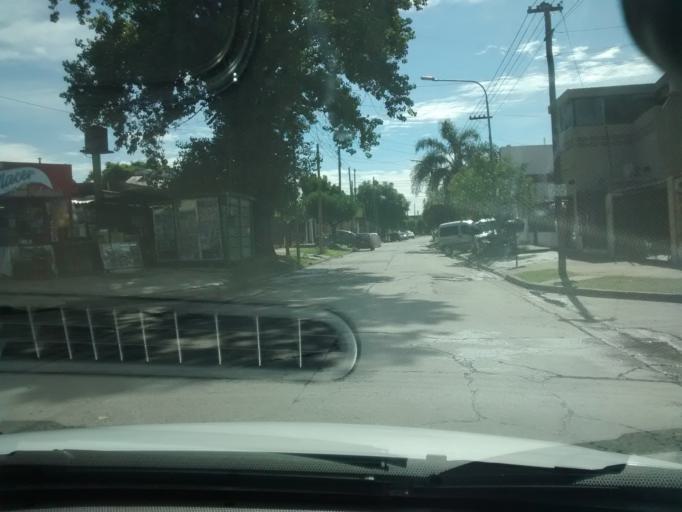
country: AR
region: Buenos Aires
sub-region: Partido de Moron
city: Moron
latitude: -34.6657
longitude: -58.6086
